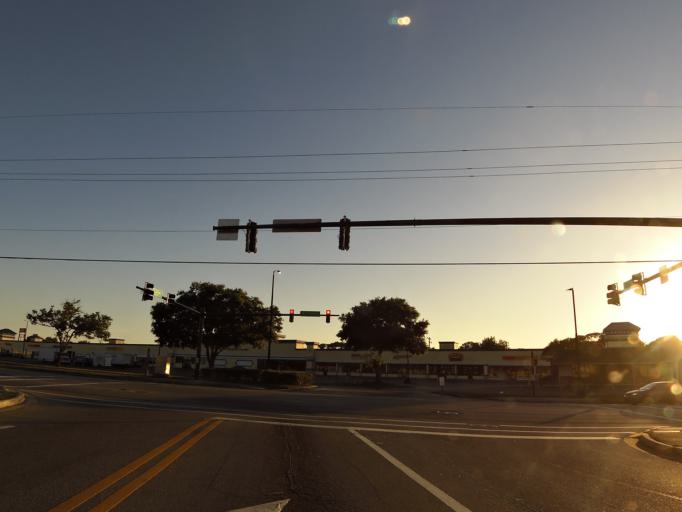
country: US
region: Florida
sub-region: Duval County
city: Jacksonville
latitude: 30.3308
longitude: -81.5874
